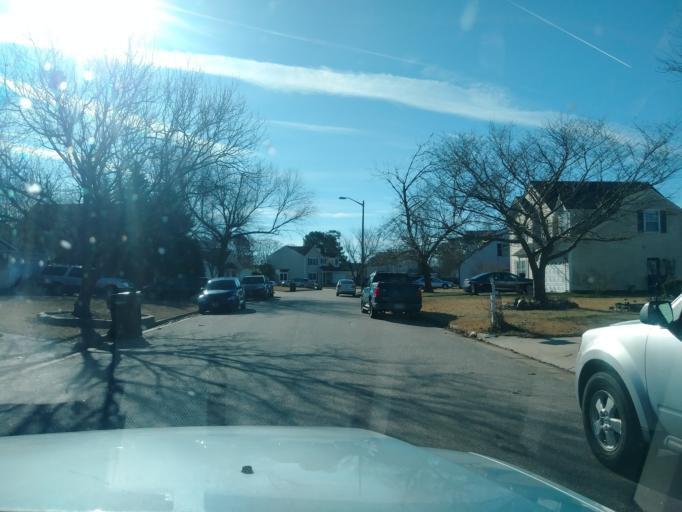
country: US
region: Virginia
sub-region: City of Chesapeake
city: Chesapeake
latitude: 36.7542
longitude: -76.2089
